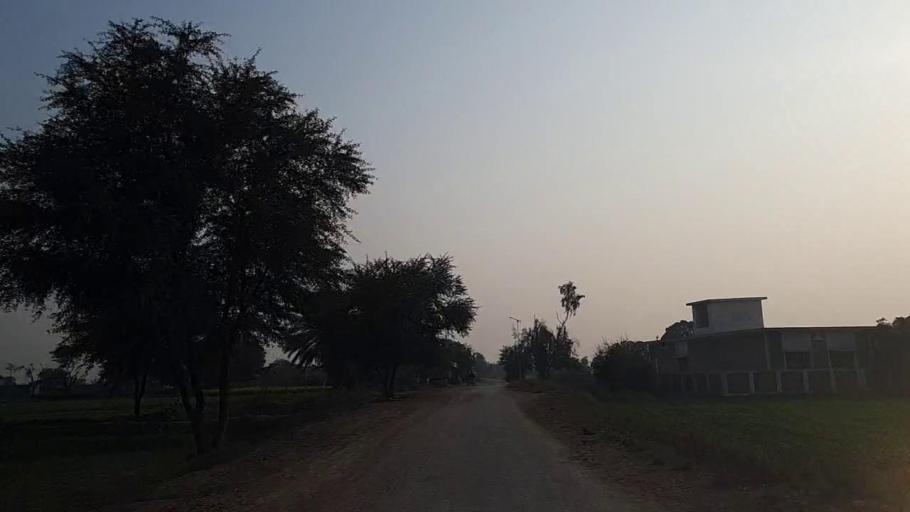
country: PK
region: Sindh
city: Nawabshah
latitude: 26.2159
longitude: 68.4729
